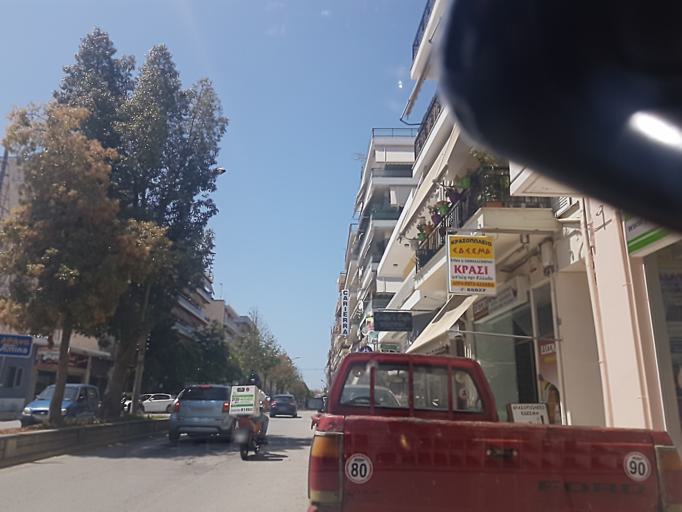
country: GR
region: Central Greece
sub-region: Nomos Evvoias
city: Chalkida
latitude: 38.4604
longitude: 23.5972
